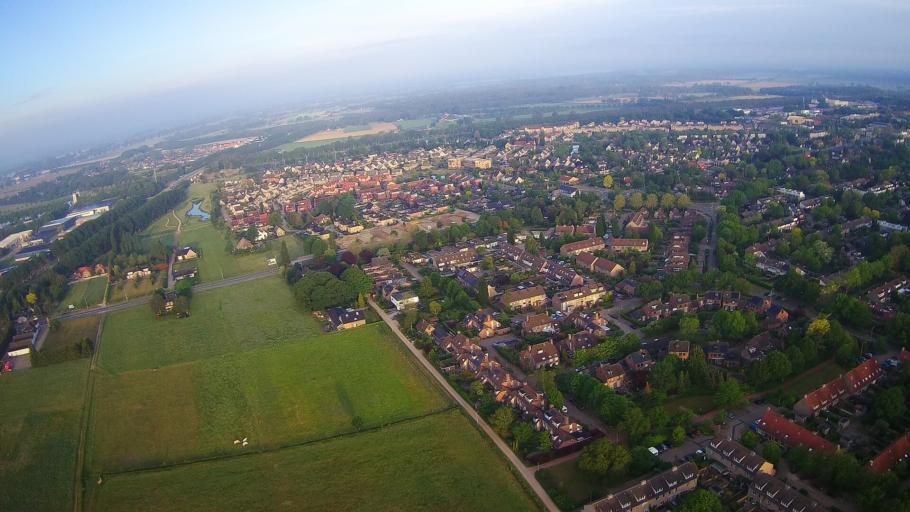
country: NL
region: North Brabant
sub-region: Gemeente Cuijk
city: Cuijk
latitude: 51.7751
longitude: 5.8660
